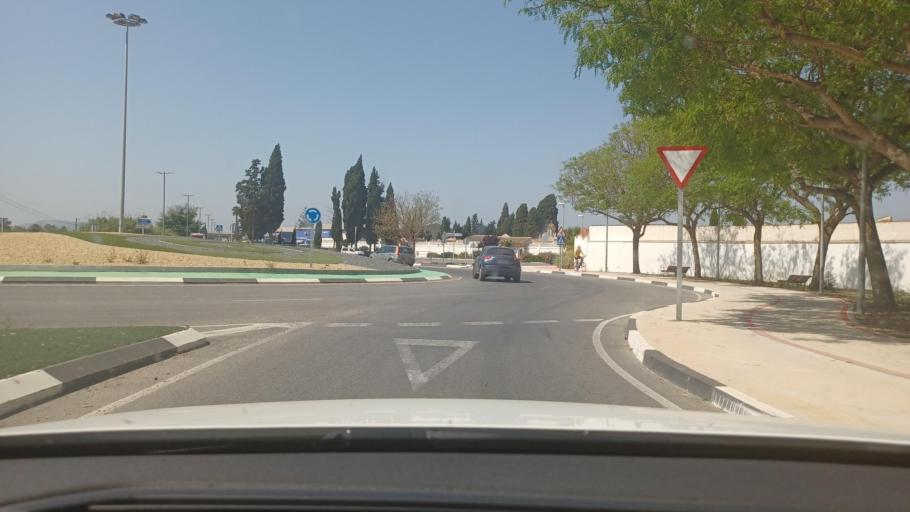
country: ES
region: Valencia
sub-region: Provincia de Alicante
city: Dolores
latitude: 38.1303
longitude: -0.7767
